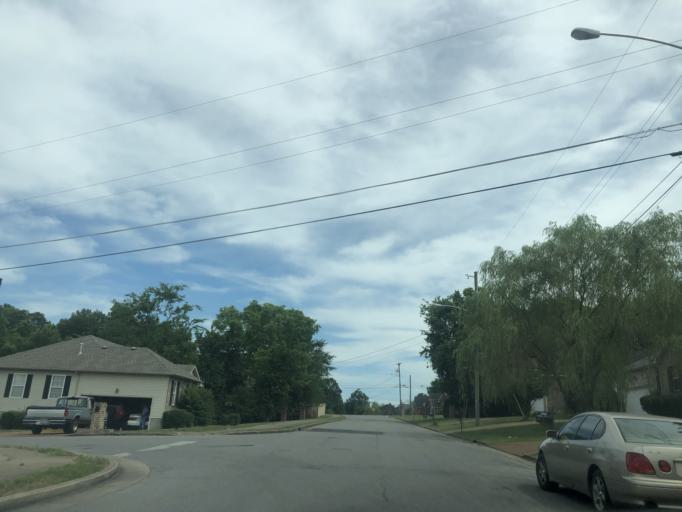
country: US
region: Tennessee
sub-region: Davidson County
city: Nashville
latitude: 36.2113
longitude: -86.8128
